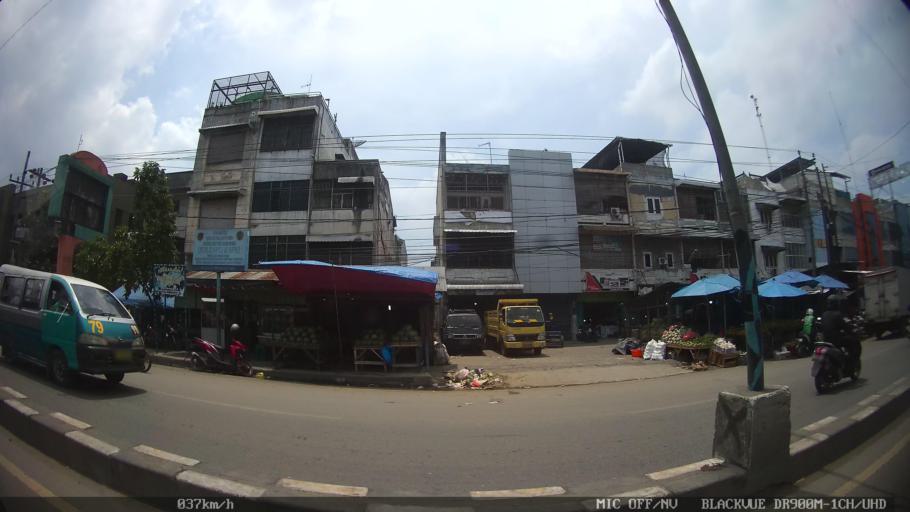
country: ID
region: North Sumatra
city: Medan
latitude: 3.6307
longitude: 98.6698
